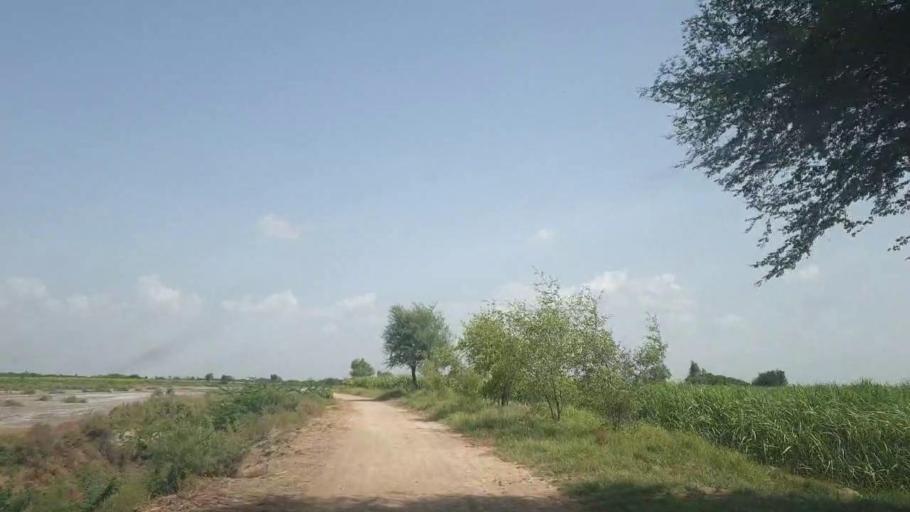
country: PK
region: Sindh
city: Tando Bago
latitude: 24.7515
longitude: 69.1763
